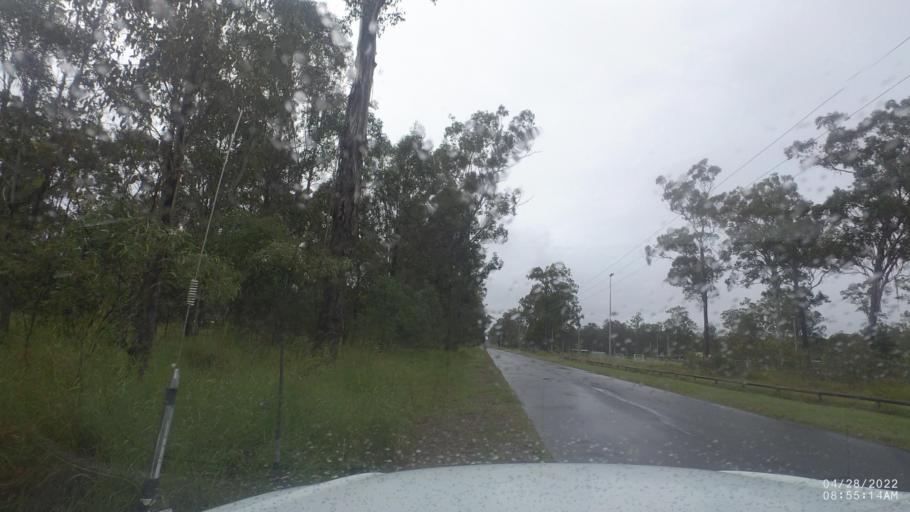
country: AU
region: Queensland
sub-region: Logan
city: Chambers Flat
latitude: -27.7882
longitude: 153.1196
